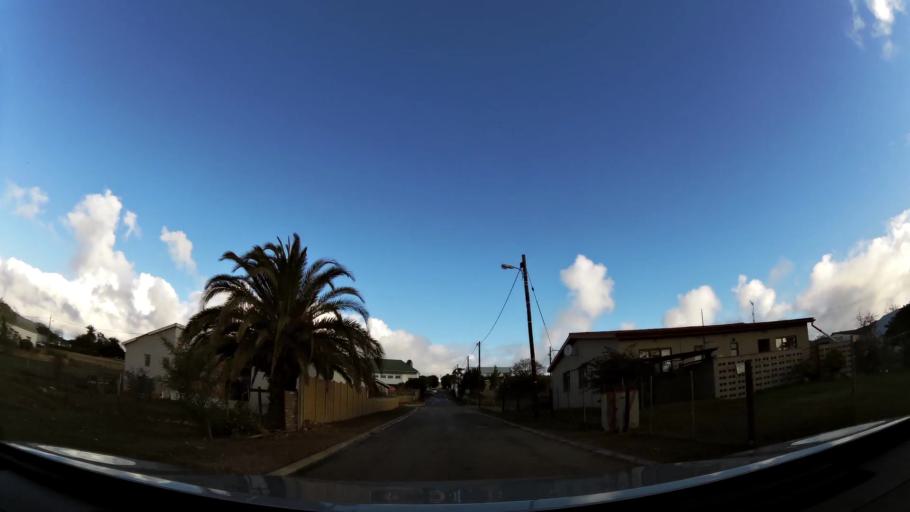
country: ZA
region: Western Cape
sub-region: Eden District Municipality
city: Riversdale
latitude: -34.2021
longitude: 21.5868
